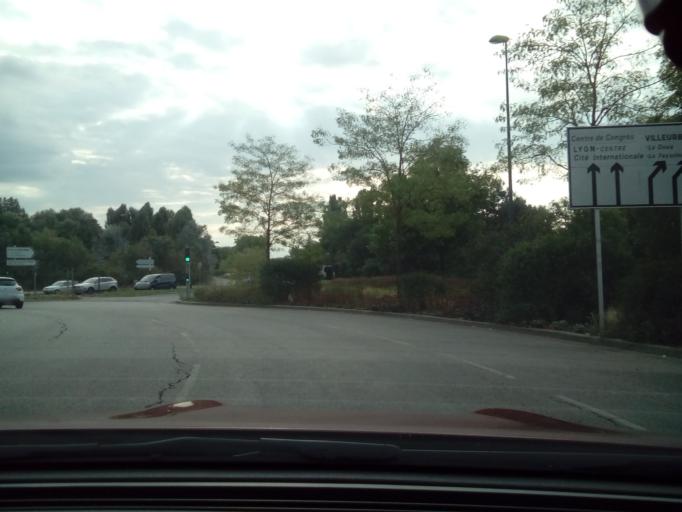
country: FR
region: Rhone-Alpes
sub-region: Departement du Rhone
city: Caluire-et-Cuire
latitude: 45.7847
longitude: 4.8633
